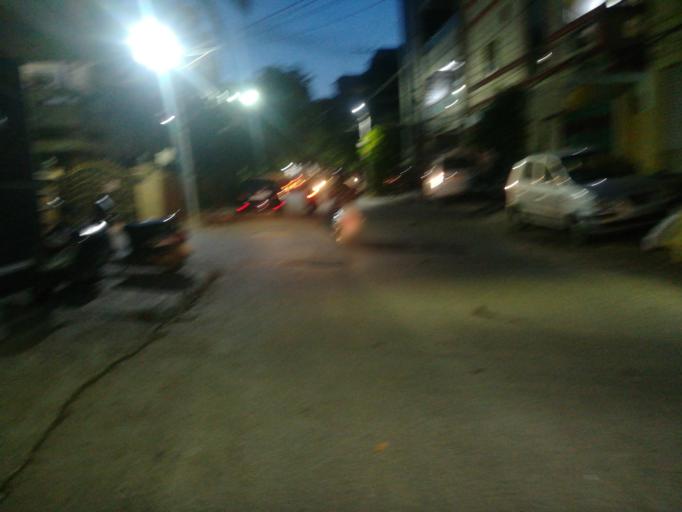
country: IN
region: Telangana
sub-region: Hyderabad
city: Malkajgiri
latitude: 17.4233
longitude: 78.5129
